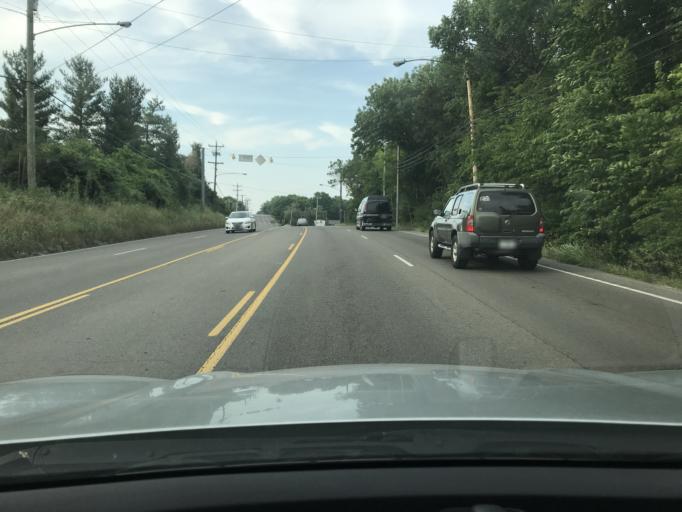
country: US
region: Tennessee
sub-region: Davidson County
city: Goodlettsville
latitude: 36.2989
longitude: -86.7224
